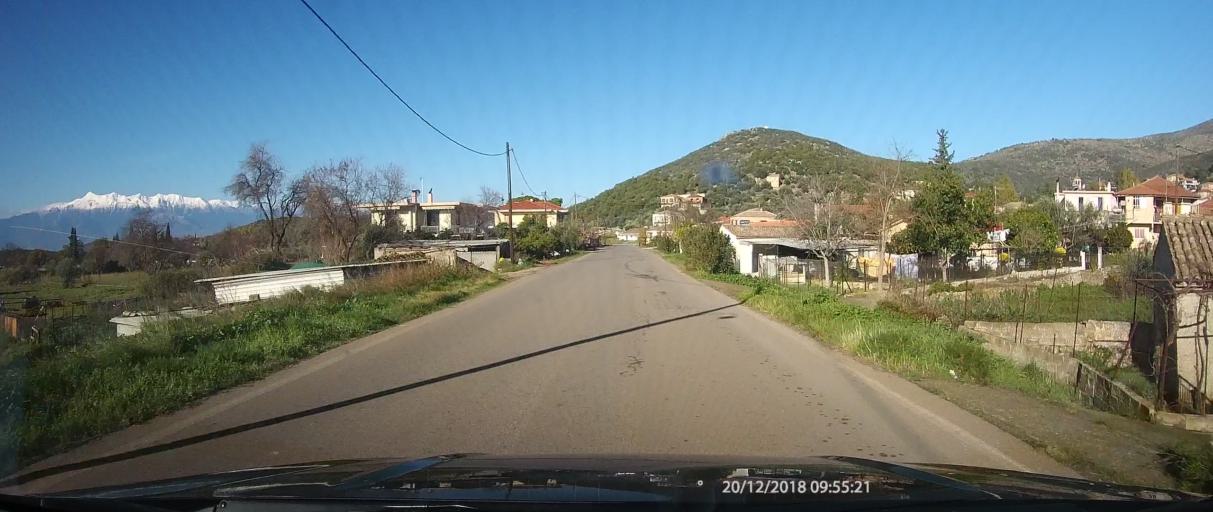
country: GR
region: Peloponnese
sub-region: Nomos Lakonias
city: Yerakion
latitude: 37.0241
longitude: 22.6237
